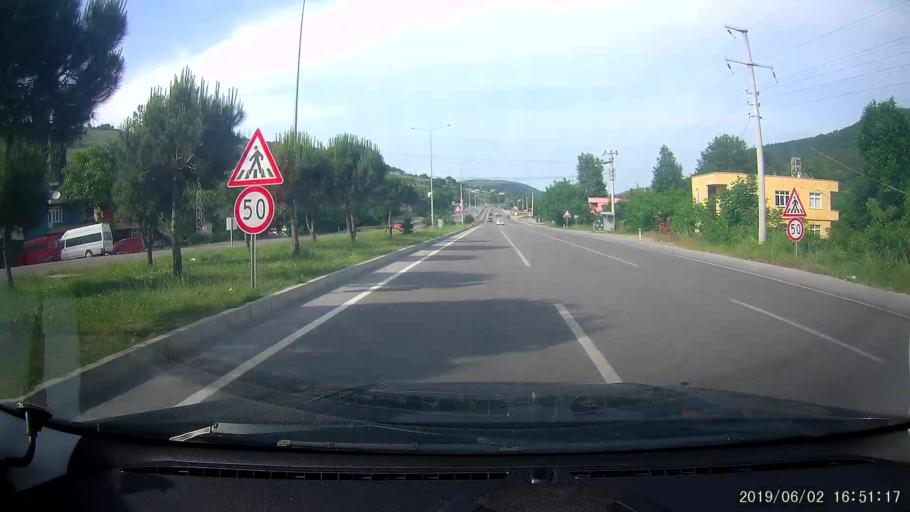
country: TR
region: Samsun
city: Taflan
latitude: 41.2715
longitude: 36.1802
